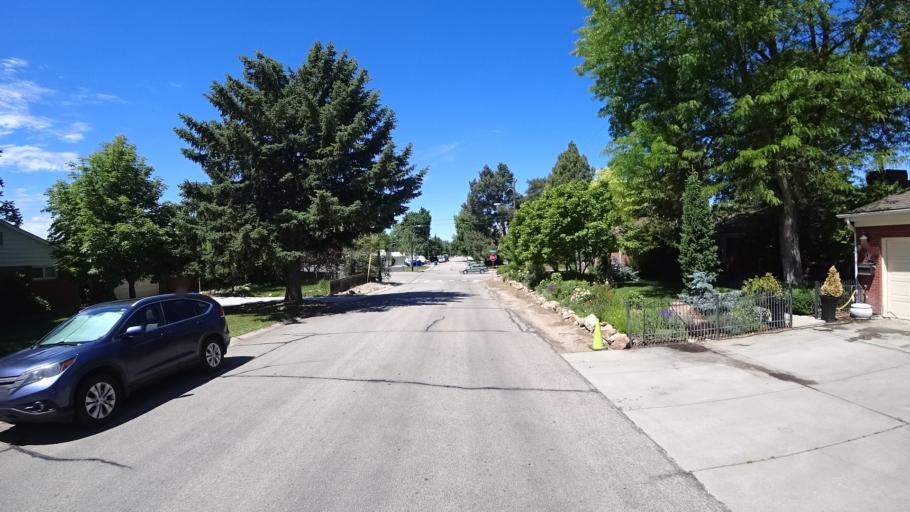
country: US
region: Idaho
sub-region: Ada County
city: Garden City
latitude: 43.5862
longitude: -116.2430
